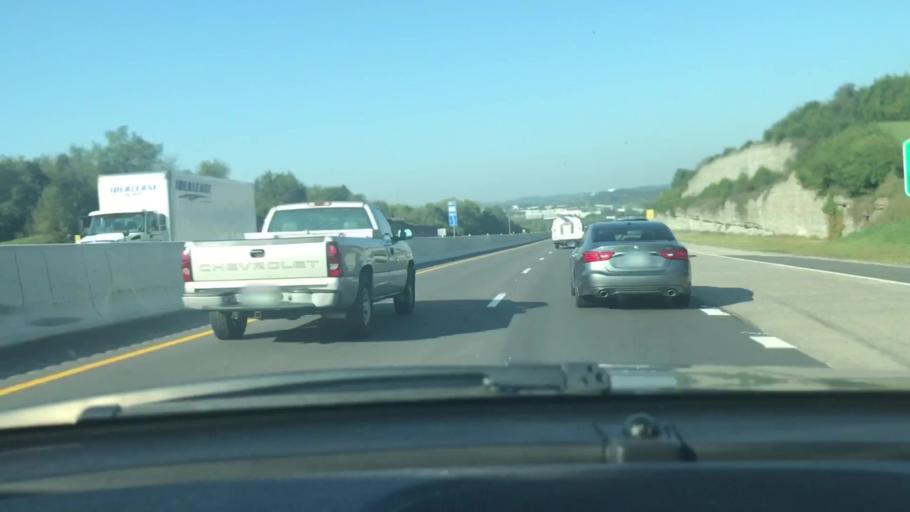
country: US
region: Tennessee
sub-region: Sumner County
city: Hendersonville
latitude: 36.3133
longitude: -86.6573
